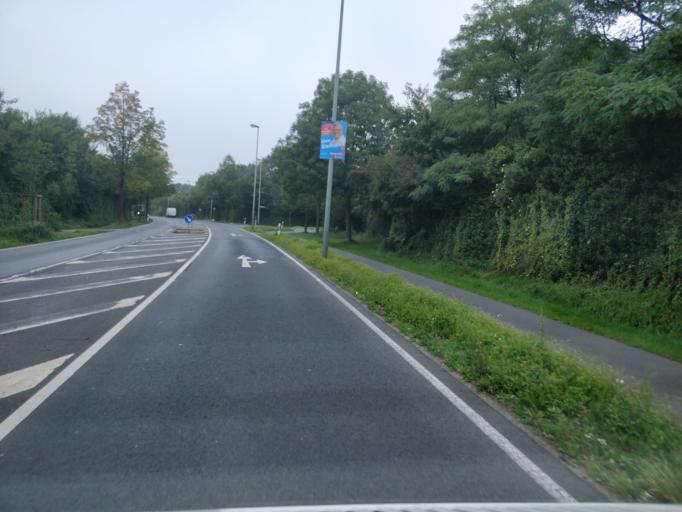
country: DE
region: North Rhine-Westphalia
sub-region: Regierungsbezirk Dusseldorf
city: Dinslaken
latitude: 51.5508
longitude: 6.7547
